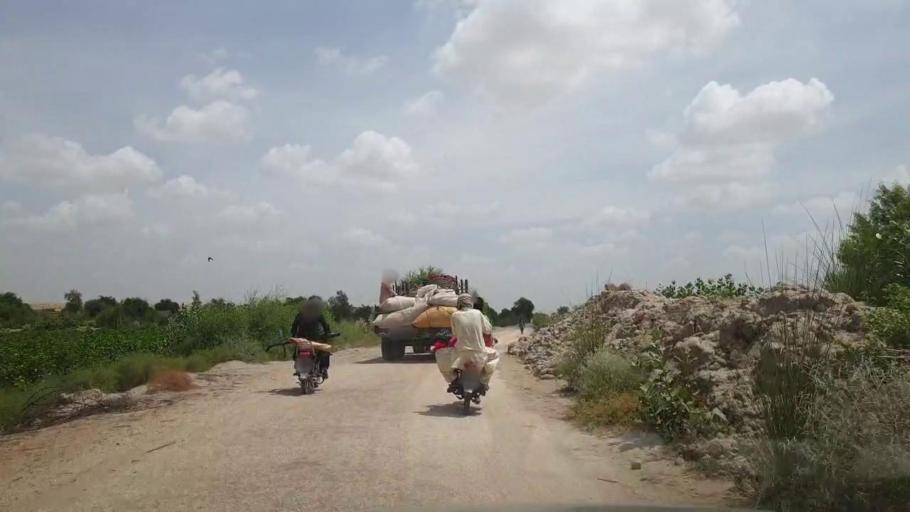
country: PK
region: Sindh
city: Kot Diji
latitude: 27.2159
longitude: 69.1105
